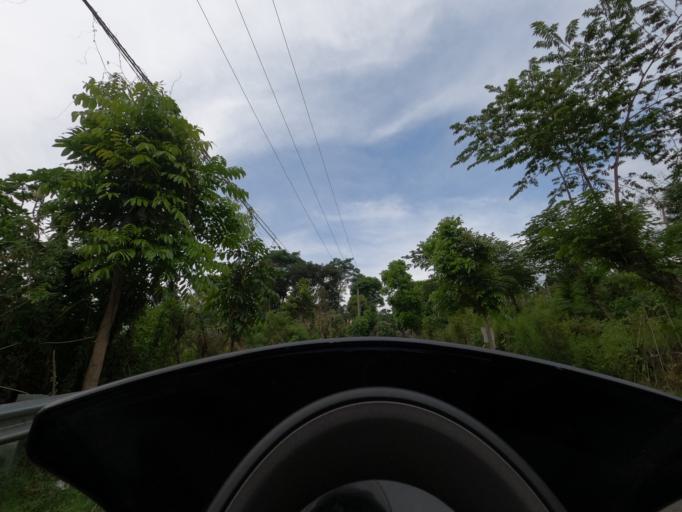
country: ID
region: West Java
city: Lembang
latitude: -6.8364
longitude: 107.6203
